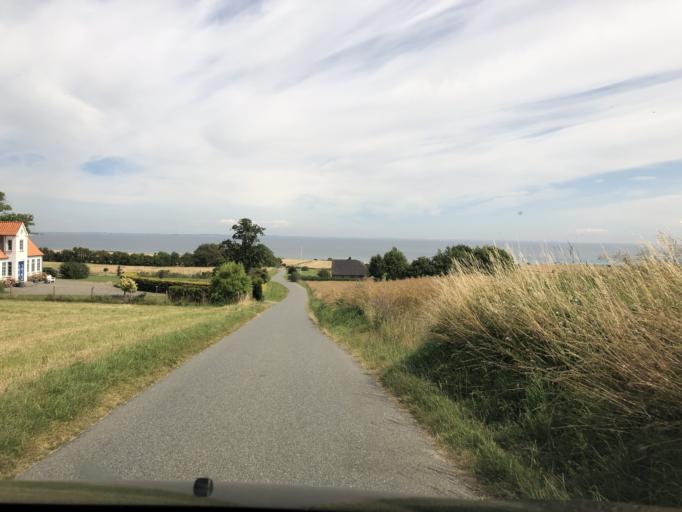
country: DK
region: South Denmark
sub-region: AEro Kommune
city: AEroskobing
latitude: 54.8322
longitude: 10.4289
